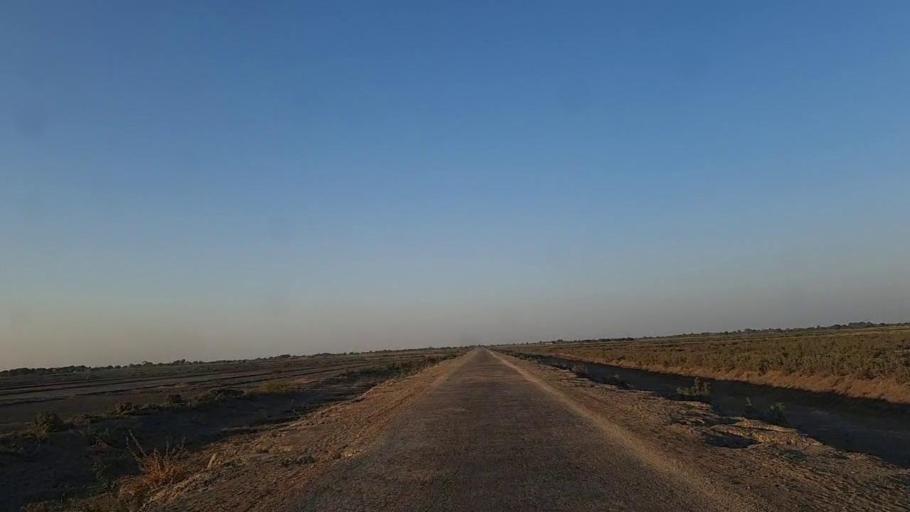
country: PK
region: Sindh
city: Naukot
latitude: 25.0133
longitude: 69.4166
